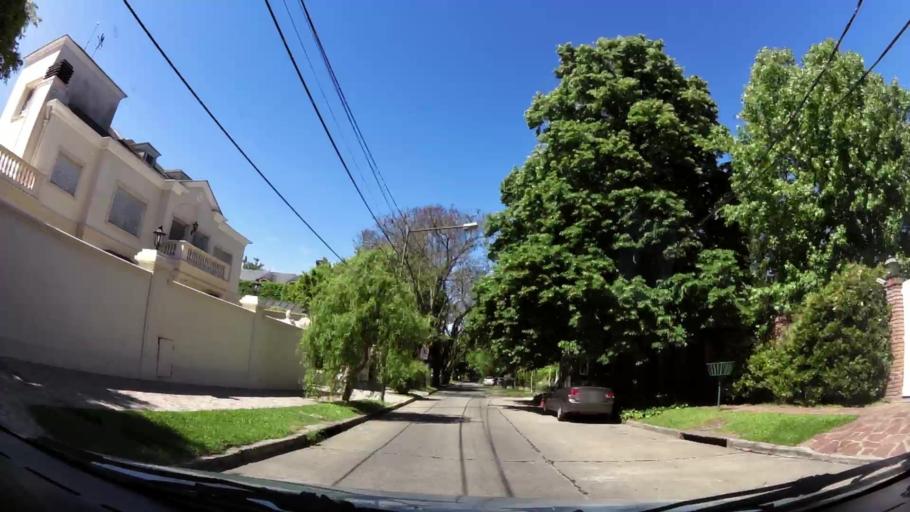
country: AR
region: Buenos Aires
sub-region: Partido de Vicente Lopez
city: Olivos
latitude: -34.4844
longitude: -58.4877
